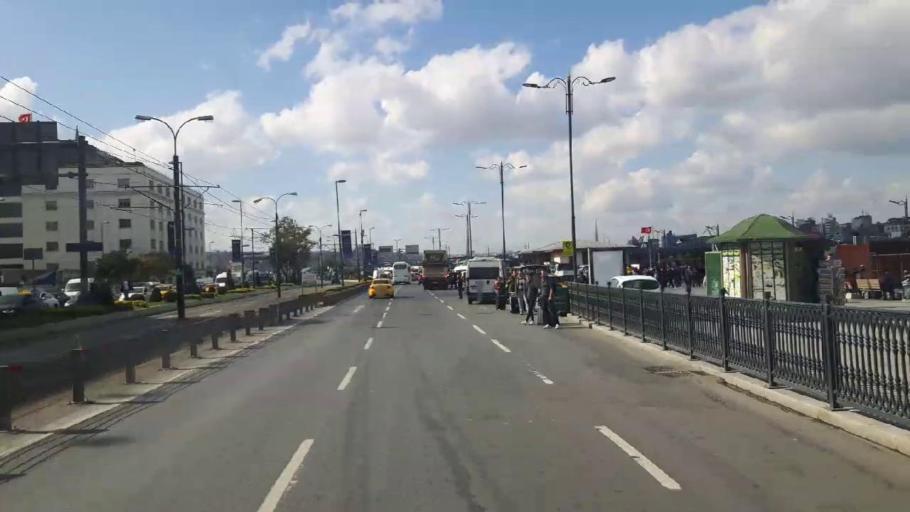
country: TR
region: Istanbul
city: Eminoenue
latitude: 41.0166
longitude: 28.9762
